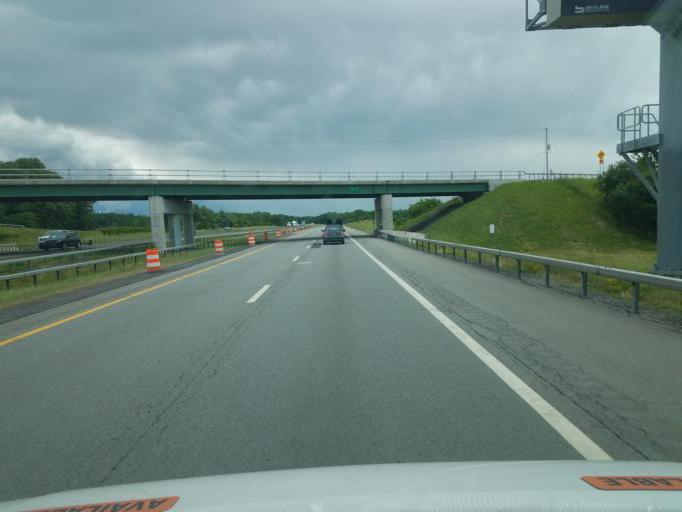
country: US
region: New York
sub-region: Ontario County
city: Phelps
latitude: 42.9623
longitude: -77.0431
